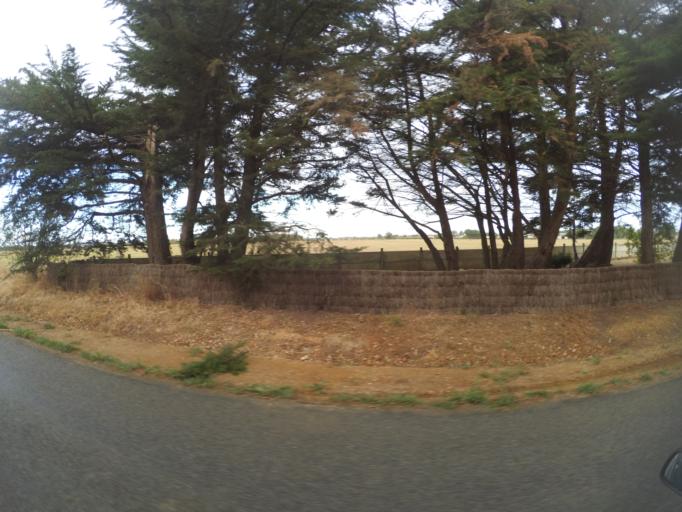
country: FR
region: Pays de la Loire
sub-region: Departement de la Loire-Atlantique
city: La Planche
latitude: 47.0226
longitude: -1.4210
